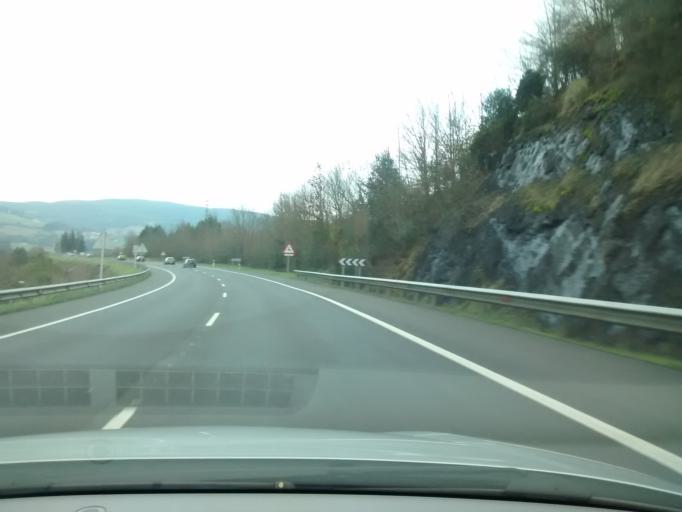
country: ES
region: Basque Country
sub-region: Bizkaia
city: Urrestieta
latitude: 43.2006
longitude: -3.1434
